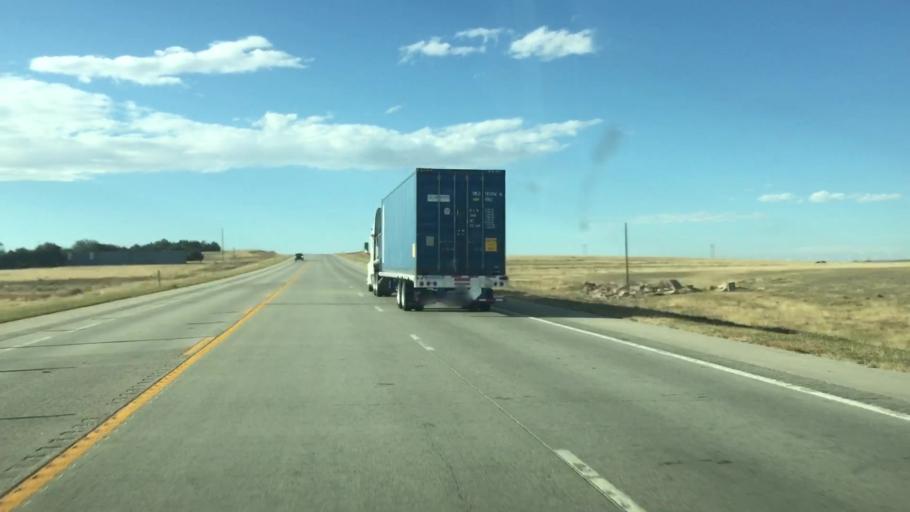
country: US
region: Colorado
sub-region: Lincoln County
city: Limon
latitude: 39.2413
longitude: -103.6241
